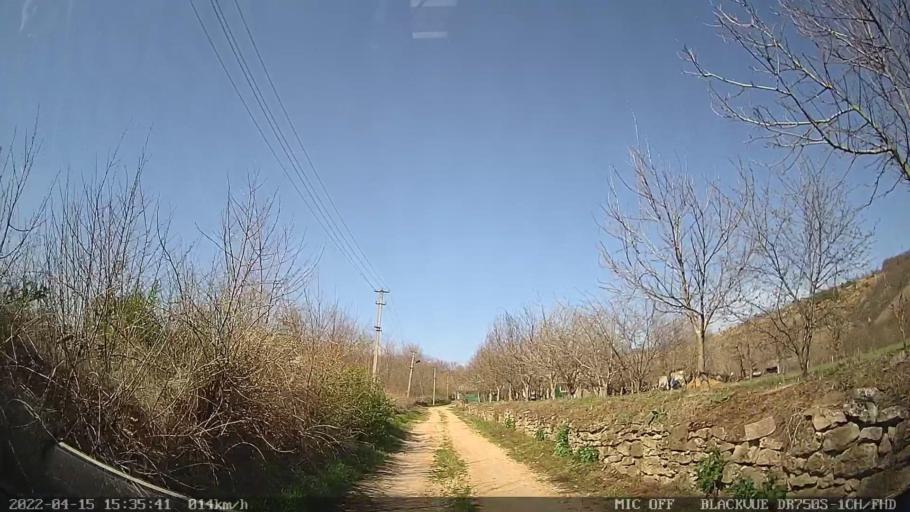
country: MD
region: Raionul Ocnita
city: Otaci
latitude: 48.3463
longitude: 27.9310
